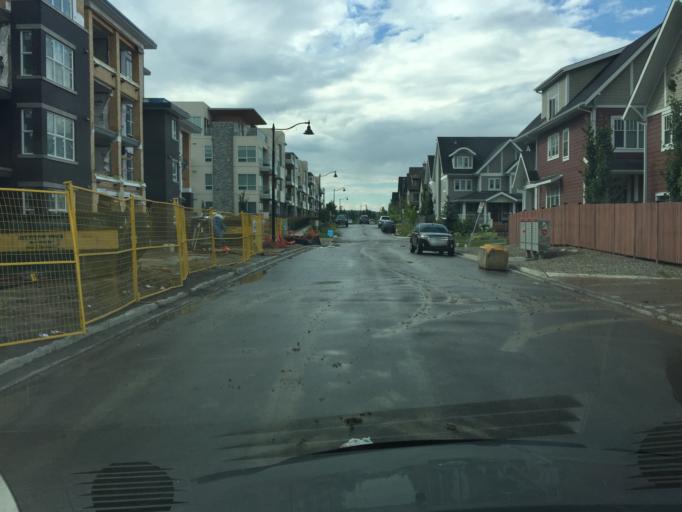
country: CA
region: Alberta
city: Calgary
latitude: 51.0159
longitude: -114.1304
